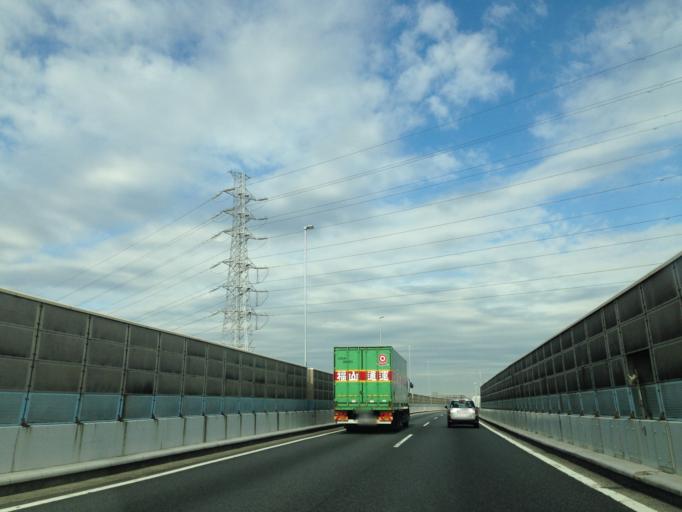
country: JP
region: Saitama
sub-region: Kawaguchi-shi
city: Hatogaya-honcho
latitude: 35.8060
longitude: 139.7591
